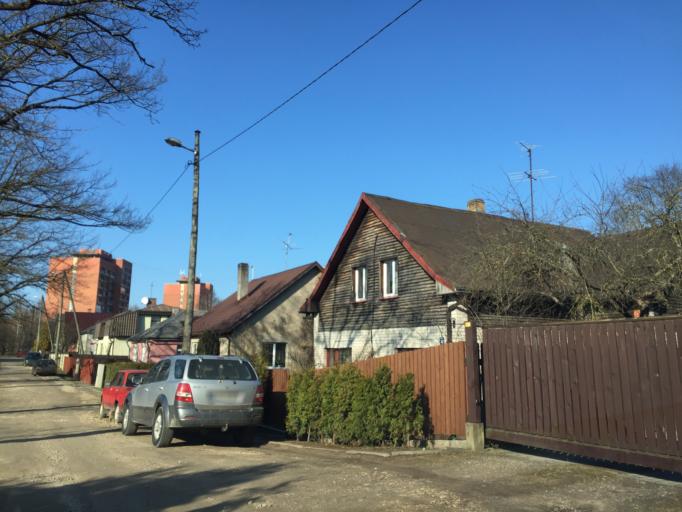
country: LV
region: Stopini
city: Ulbroka
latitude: 56.9741
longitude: 24.2436
